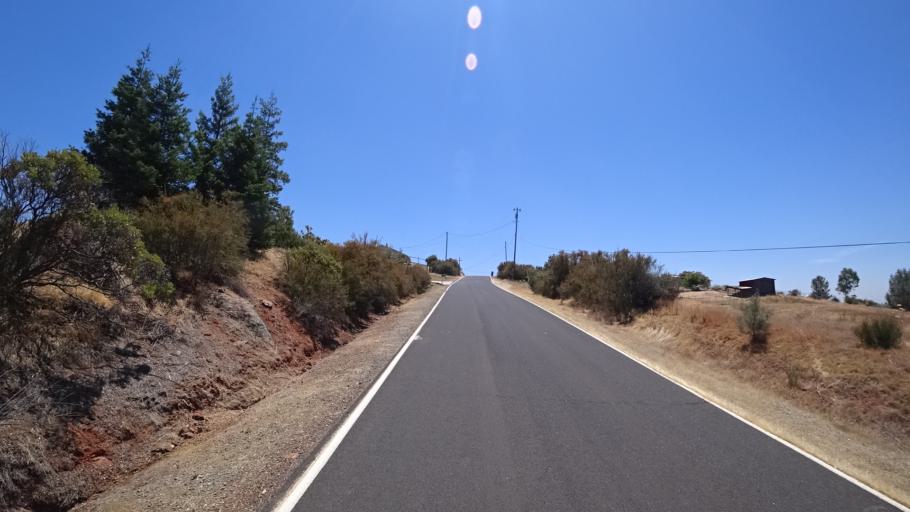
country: US
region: California
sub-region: Calaveras County
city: Rancho Calaveras
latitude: 38.1243
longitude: -120.8514
